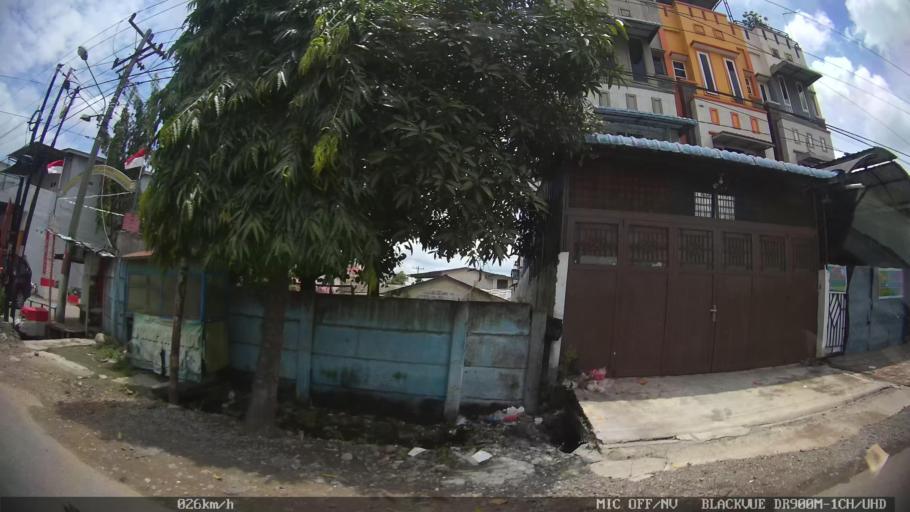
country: ID
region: North Sumatra
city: Medan
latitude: 3.5992
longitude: 98.7119
